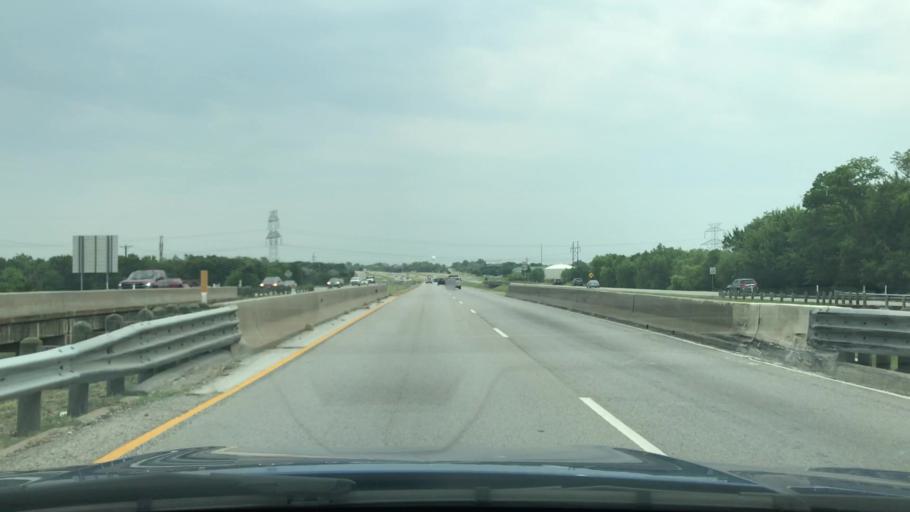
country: US
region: Texas
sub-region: Kaufman County
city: Forney
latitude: 32.7673
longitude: -96.4863
